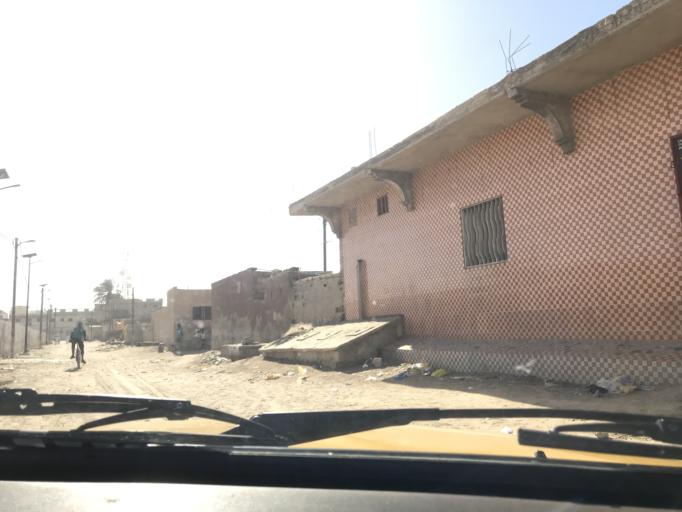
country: SN
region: Saint-Louis
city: Saint-Louis
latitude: 16.0096
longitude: -16.4872
